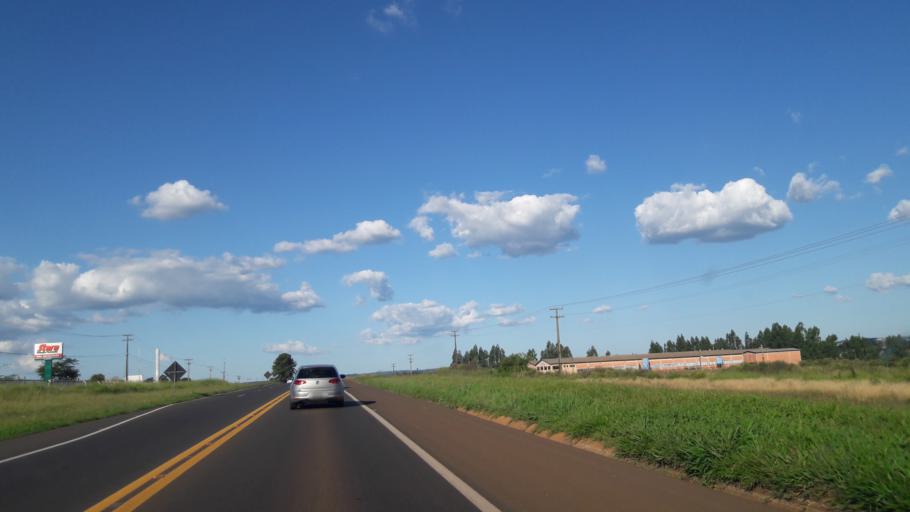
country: BR
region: Parana
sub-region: Guarapuava
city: Guarapuava
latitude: -25.3824
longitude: -51.5110
